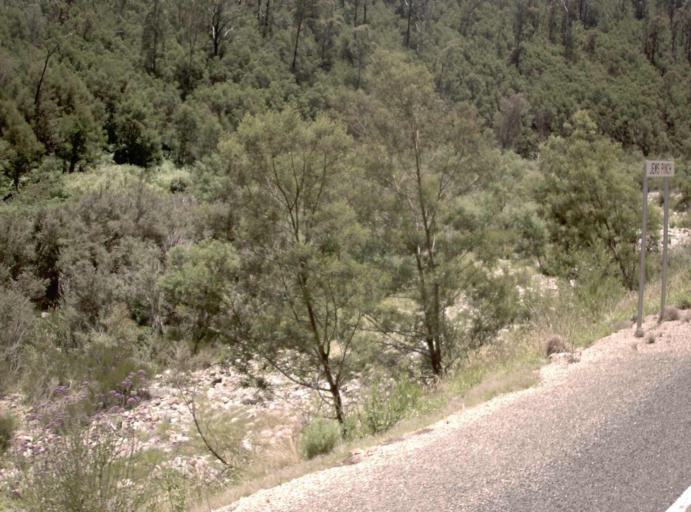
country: AU
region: Victoria
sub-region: East Gippsland
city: Bairnsdale
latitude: -37.5288
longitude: 147.8461
